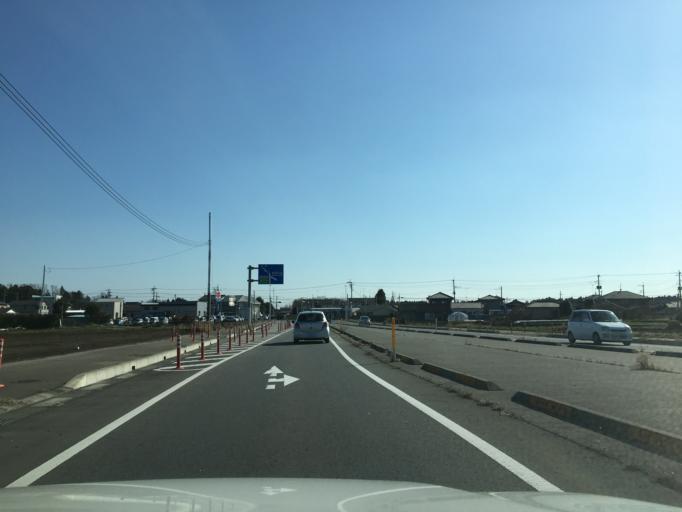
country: JP
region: Ibaraki
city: Omiya
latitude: 36.4791
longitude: 140.3810
